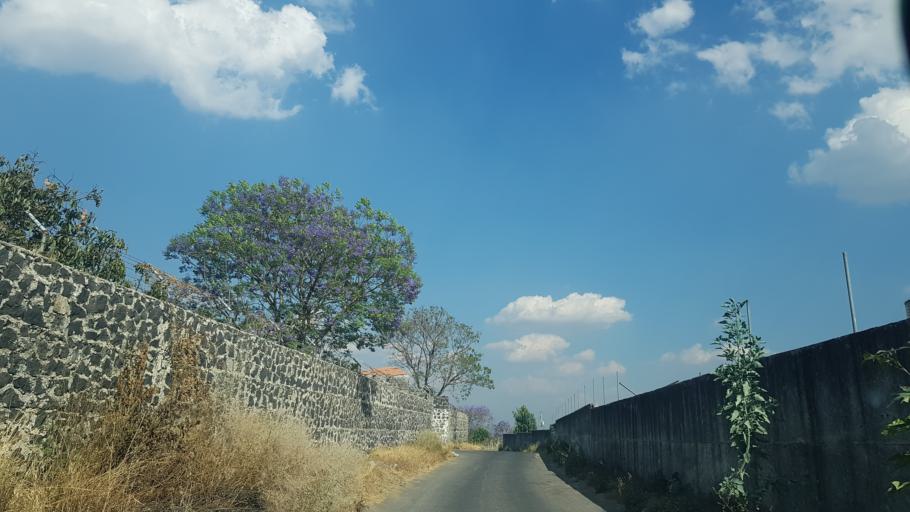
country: MX
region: Puebla
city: Atlixco
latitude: 18.8820
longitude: -98.4902
